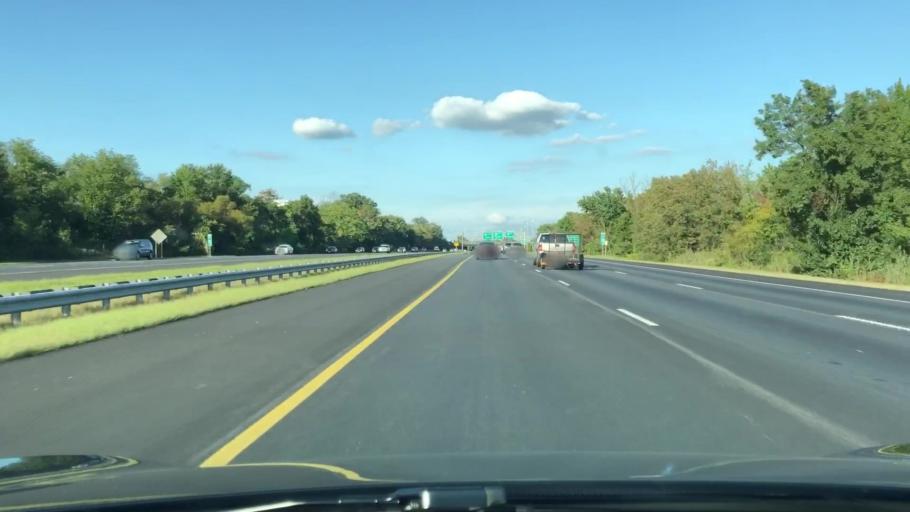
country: US
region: New Jersey
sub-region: Burlington County
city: Mount Laurel
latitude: 39.9619
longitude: -74.9161
